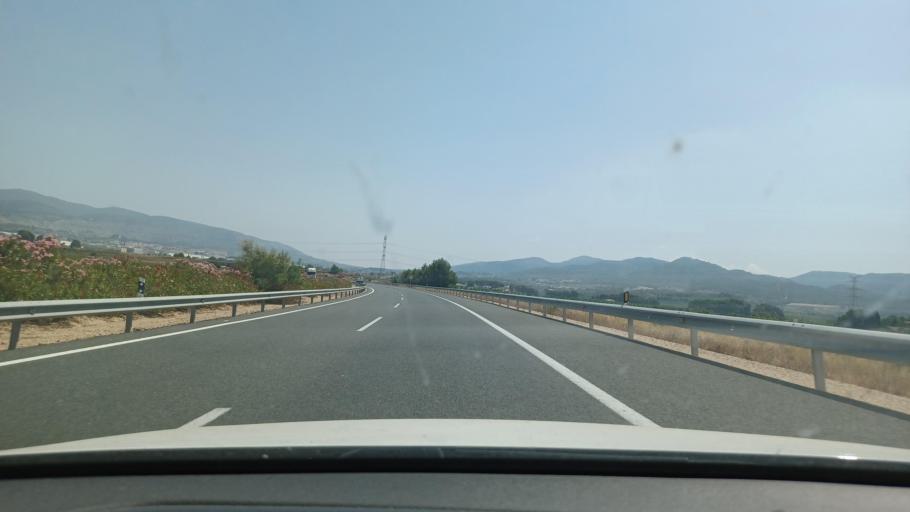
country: ES
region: Valencia
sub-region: Provincia de Alicante
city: Ibi
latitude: 38.5933
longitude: -0.6165
